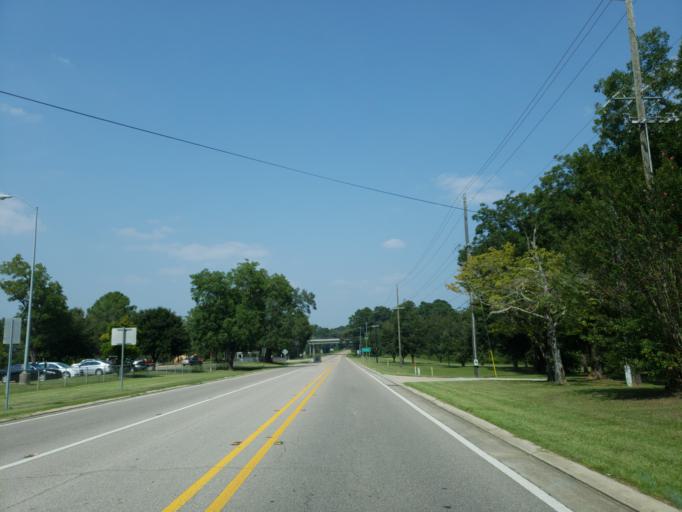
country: US
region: Mississippi
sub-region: Jones County
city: Ellisville
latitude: 31.5878
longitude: -89.2143
